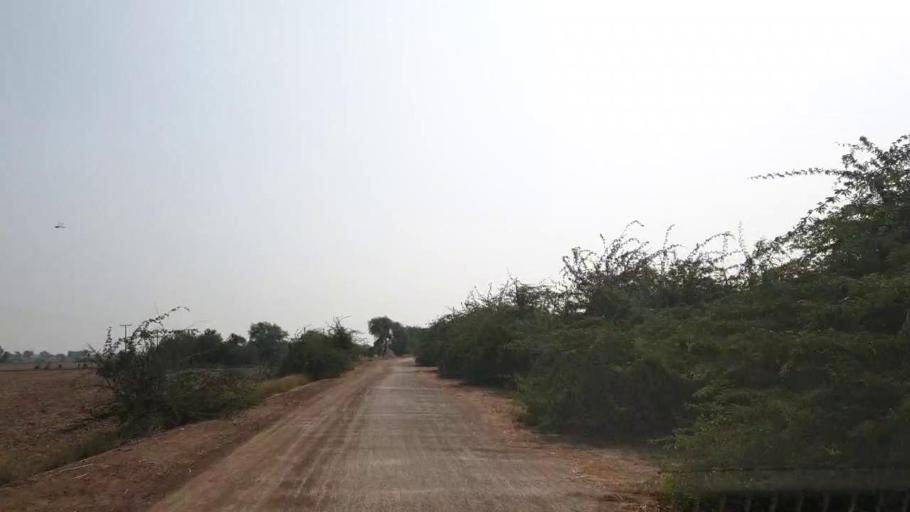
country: PK
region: Sindh
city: Matli
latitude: 24.9876
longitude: 68.5798
